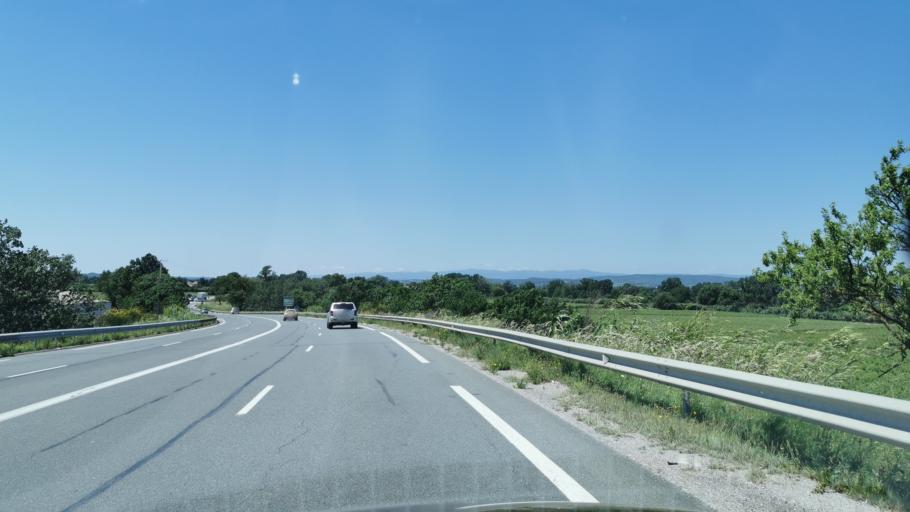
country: FR
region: Languedoc-Roussillon
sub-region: Departement de l'Aude
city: Nevian
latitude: 43.2117
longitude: 2.8736
